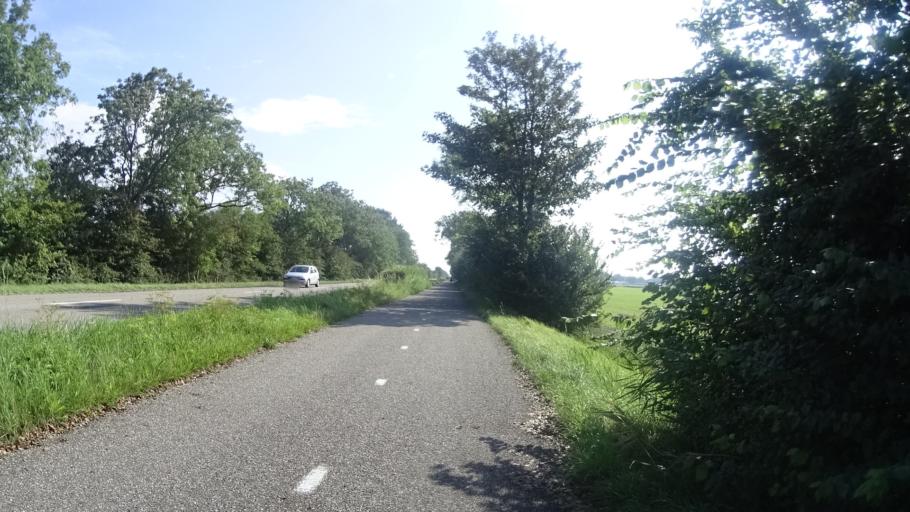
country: NL
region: Friesland
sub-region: Gemeente Franekeradeel
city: Tzum
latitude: 53.1920
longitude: 5.5890
